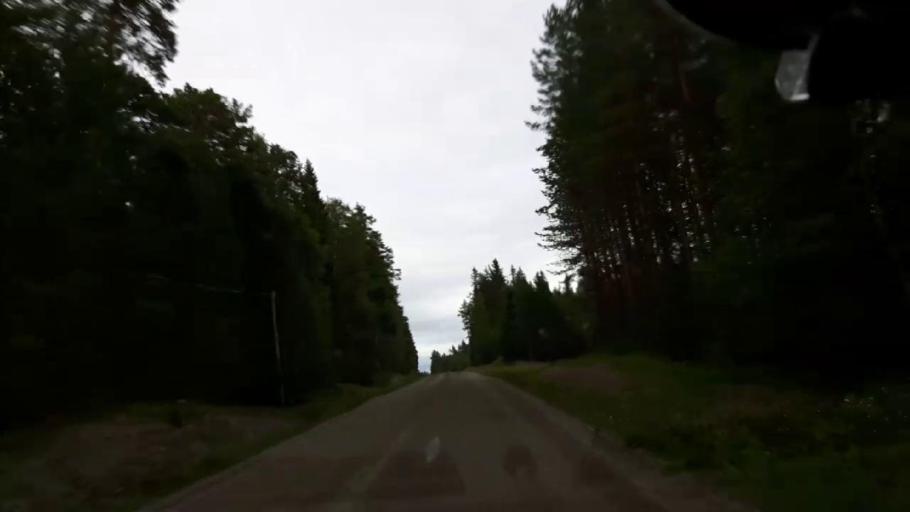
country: SE
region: Jaemtland
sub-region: Braecke Kommun
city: Braecke
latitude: 62.9196
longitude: 15.5597
